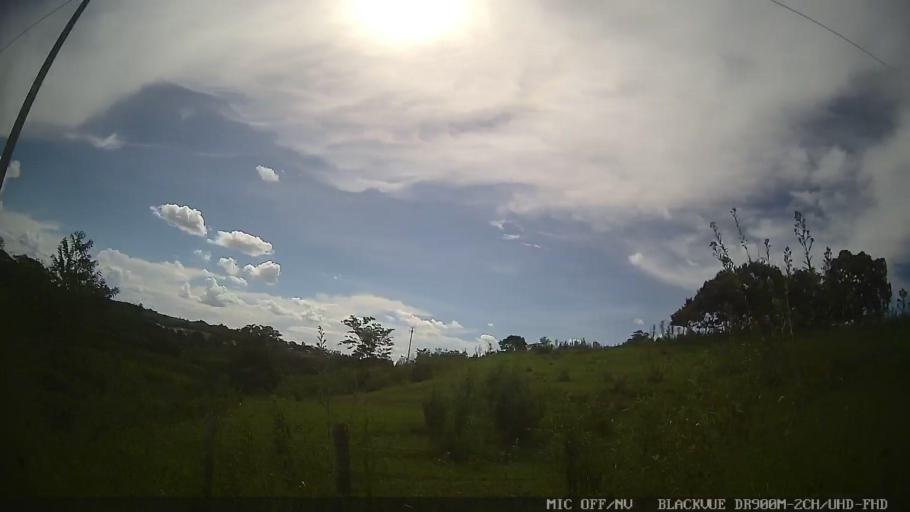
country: BR
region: Sao Paulo
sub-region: Conchas
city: Conchas
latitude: -23.0013
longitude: -48.0000
